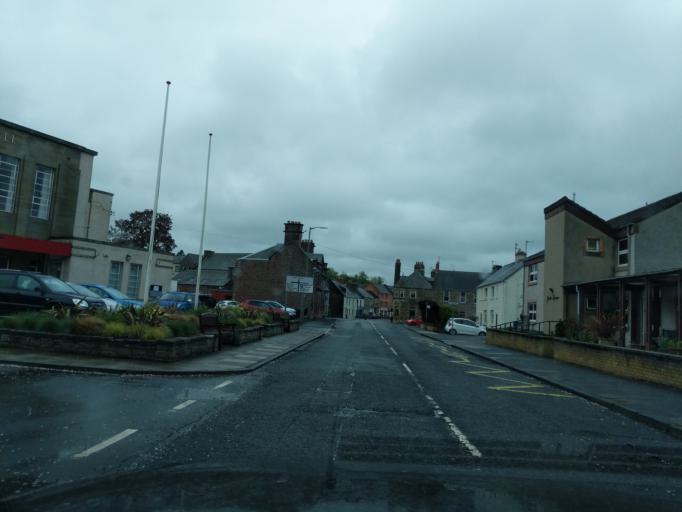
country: GB
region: Scotland
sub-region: The Scottish Borders
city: Kelso
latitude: 55.6009
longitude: -2.4307
